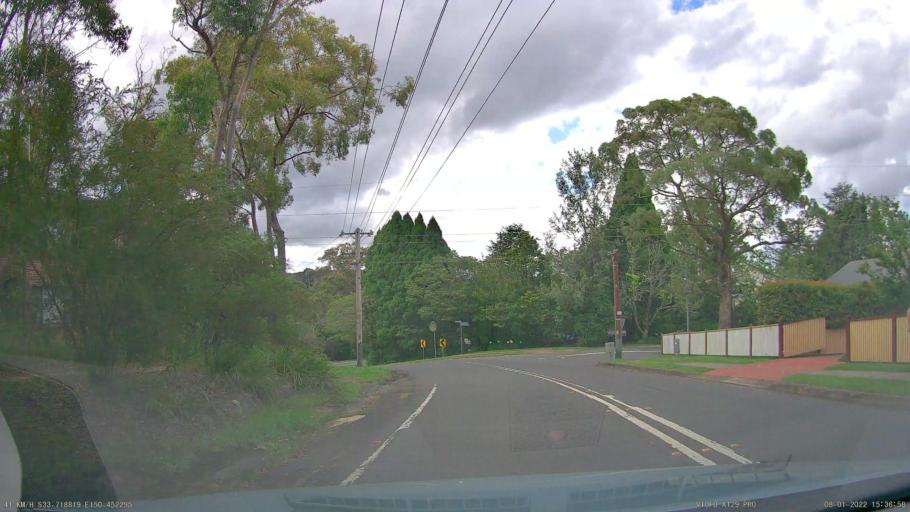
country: AU
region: New South Wales
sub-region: Blue Mountains Municipality
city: Hazelbrook
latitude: -33.7187
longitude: 150.4523
